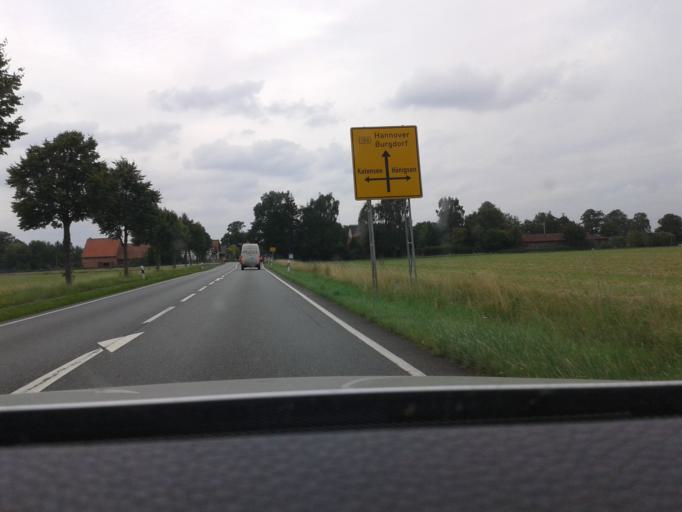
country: DE
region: Lower Saxony
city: Haenigsen
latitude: 52.4601
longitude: 10.1367
